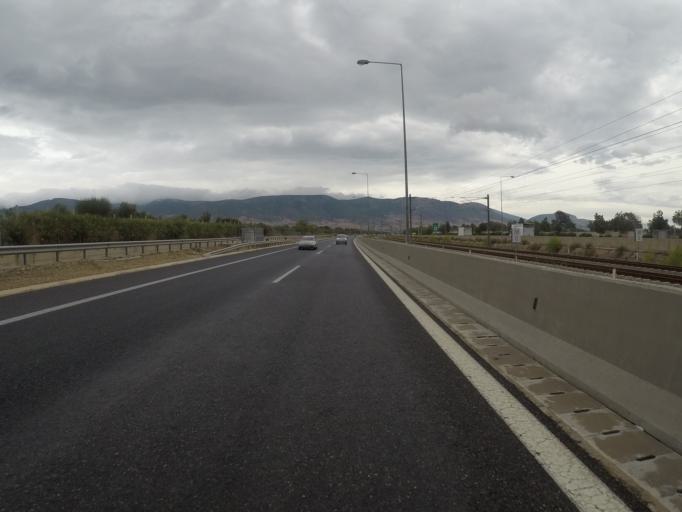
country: GR
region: Attica
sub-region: Nomarchia Dytikis Attikis
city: Magoula
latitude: 38.0867
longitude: 23.5444
